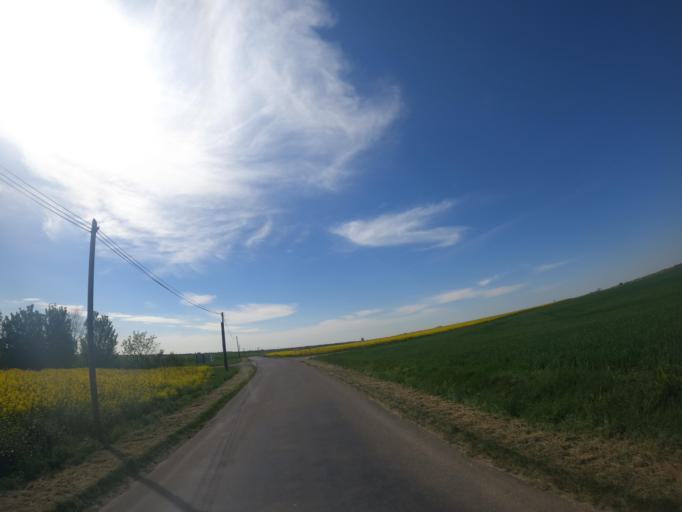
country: FR
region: Poitou-Charentes
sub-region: Departement des Deux-Sevres
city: Saint-Varent
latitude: 46.8887
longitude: -0.1640
